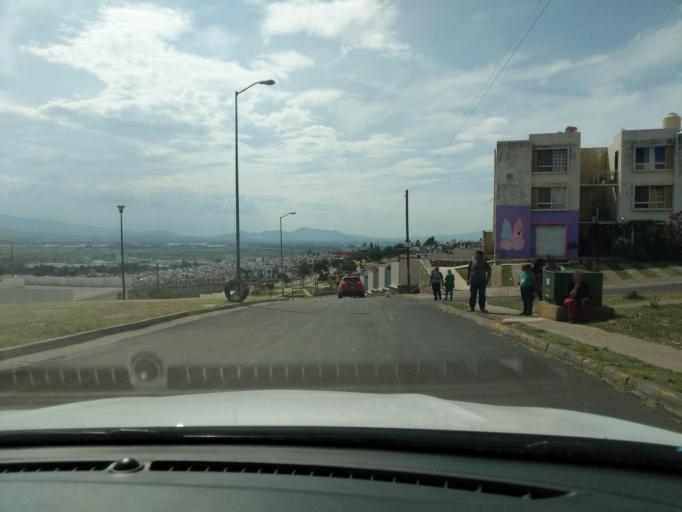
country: MX
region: Jalisco
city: San Jose del Castillo
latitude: 20.5214
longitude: -103.2273
